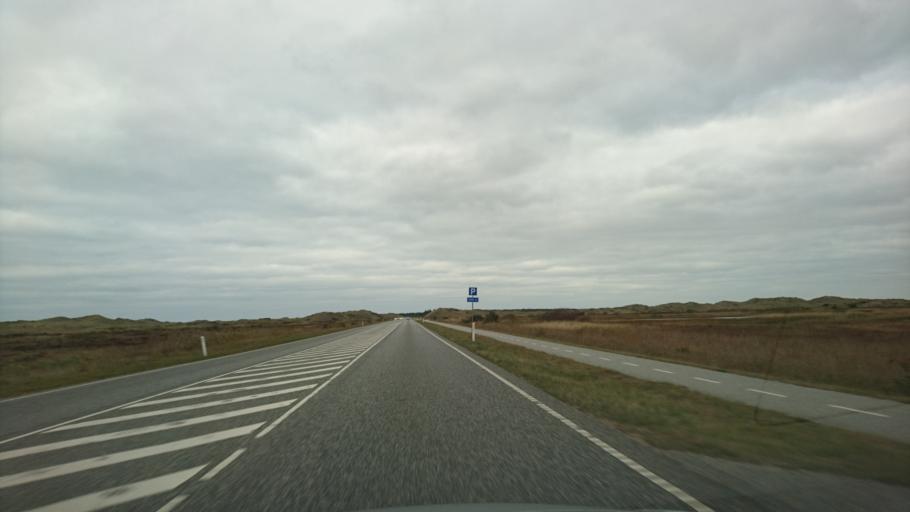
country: DK
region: North Denmark
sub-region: Frederikshavn Kommune
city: Skagen
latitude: 57.6864
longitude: 10.4679
